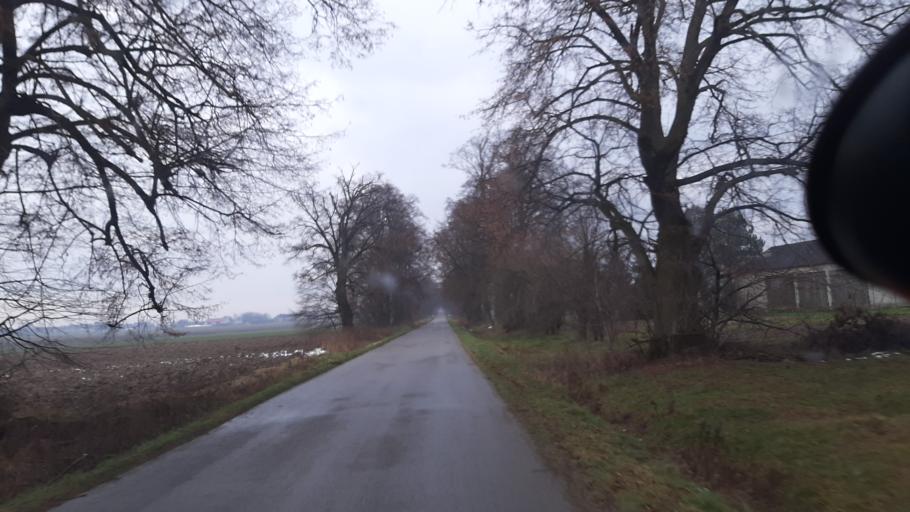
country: PL
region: Lublin Voivodeship
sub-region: Powiat lubelski
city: Jastkow
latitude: 51.3440
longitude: 22.5279
